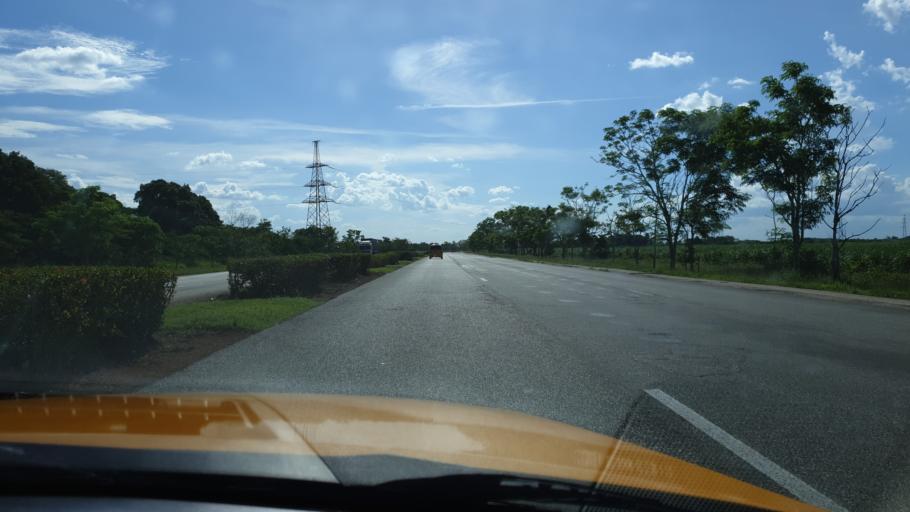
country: CU
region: Cienfuegos
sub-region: Municipio de Aguada de Pasajeros
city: Aguada de Pasajeros
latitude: 22.4086
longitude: -80.8847
